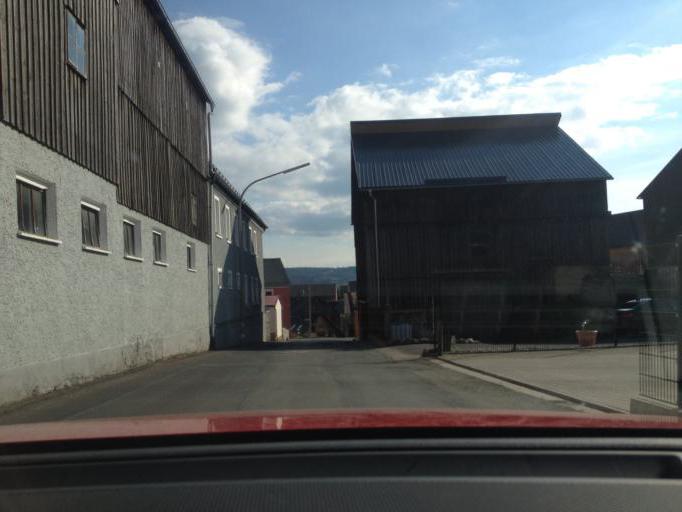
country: DE
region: Bavaria
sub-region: Upper Franconia
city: Arzberg
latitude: 50.0340
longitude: 12.1582
